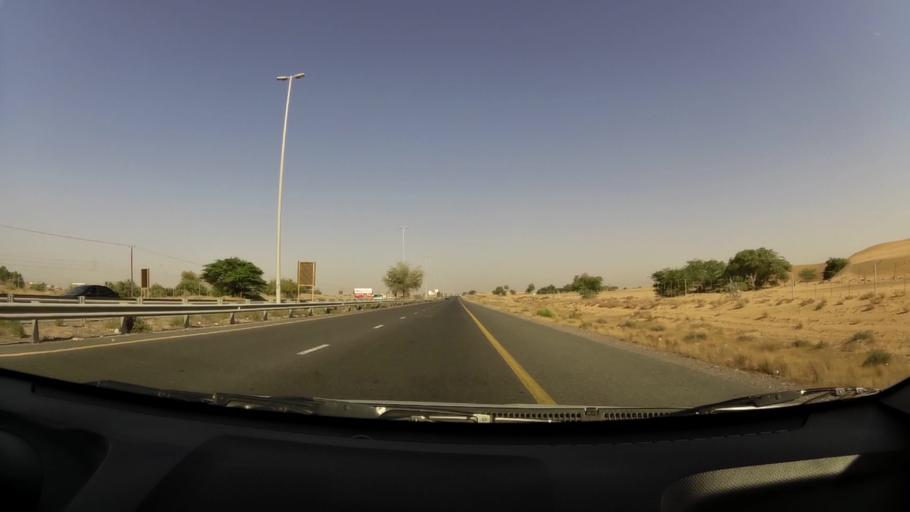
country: AE
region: Umm al Qaywayn
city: Umm al Qaywayn
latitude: 25.4662
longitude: 55.5935
